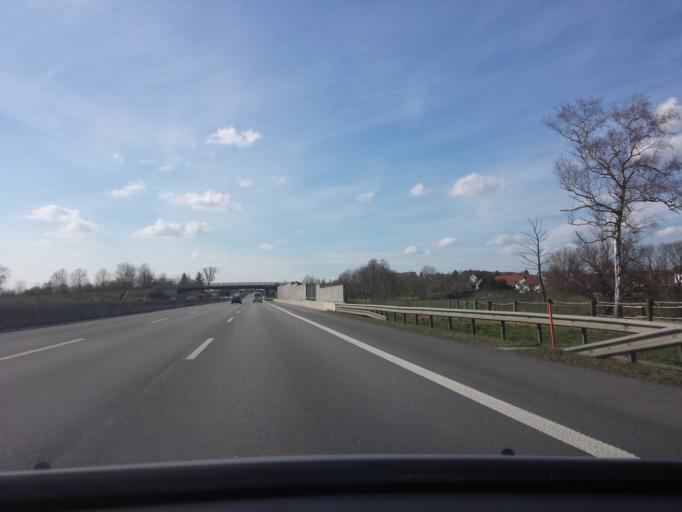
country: DE
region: Bavaria
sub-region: Upper Bavaria
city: Bergkirchen
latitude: 48.2494
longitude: 11.3173
